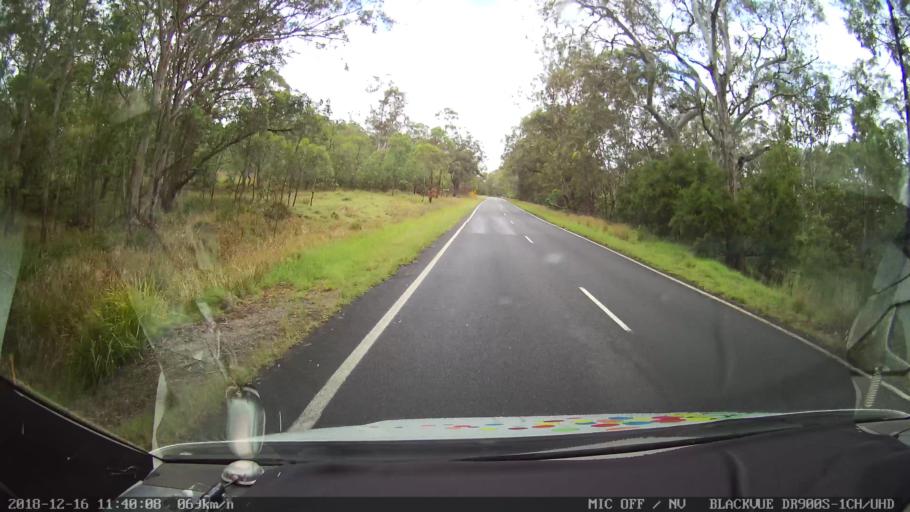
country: AU
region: New South Wales
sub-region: Tenterfield Municipality
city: Carrolls Creek
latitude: -28.9617
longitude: 152.1958
